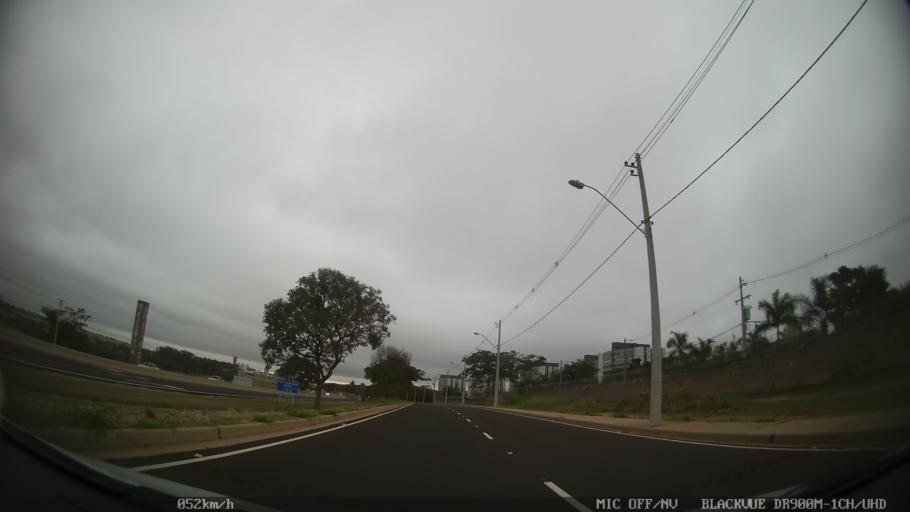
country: BR
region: Sao Paulo
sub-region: Sao Jose Do Rio Preto
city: Sao Jose do Rio Preto
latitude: -20.8512
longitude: -49.3997
